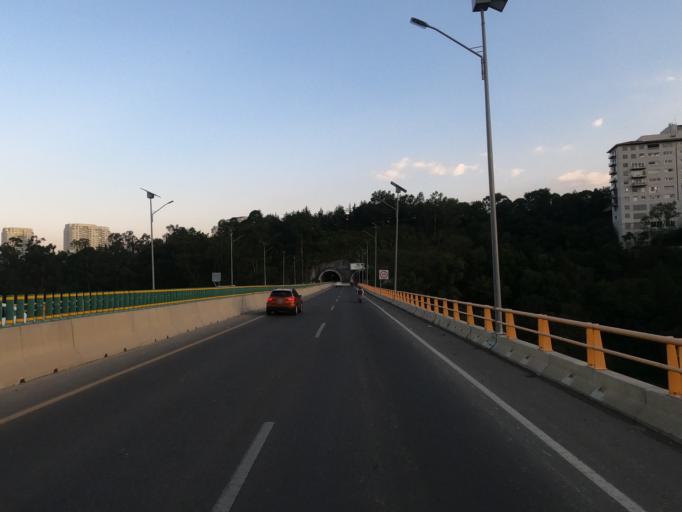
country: MX
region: Mexico
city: San Bartolome Coatepec
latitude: 19.4133
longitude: -99.2852
